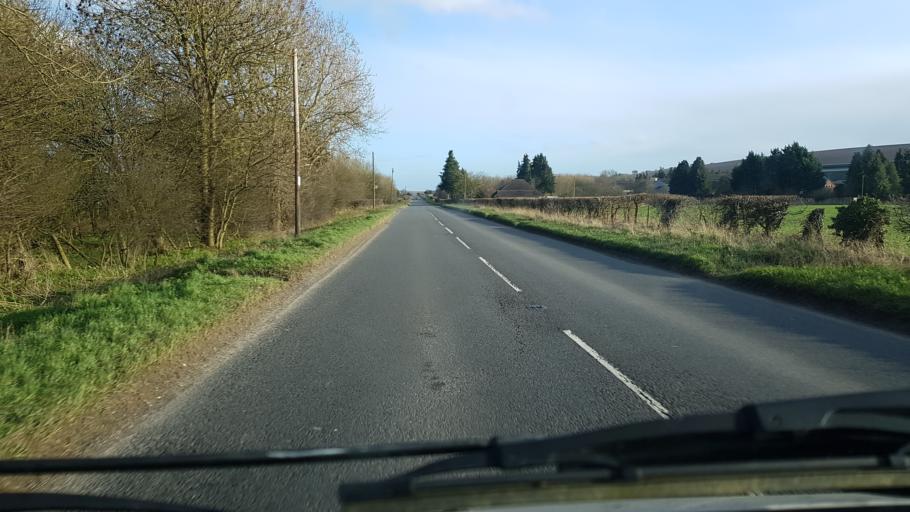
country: GB
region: England
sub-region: Wiltshire
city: Burbage
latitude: 51.3242
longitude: -1.6755
